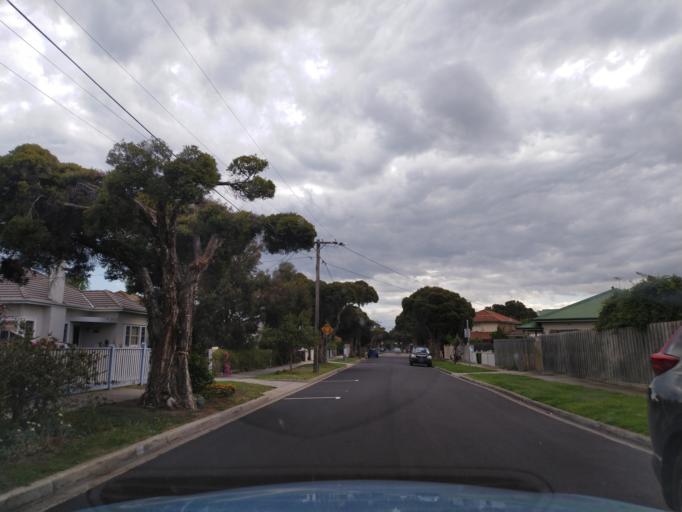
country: AU
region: Victoria
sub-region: Hobsons Bay
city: Newport
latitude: -37.8468
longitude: 144.8774
